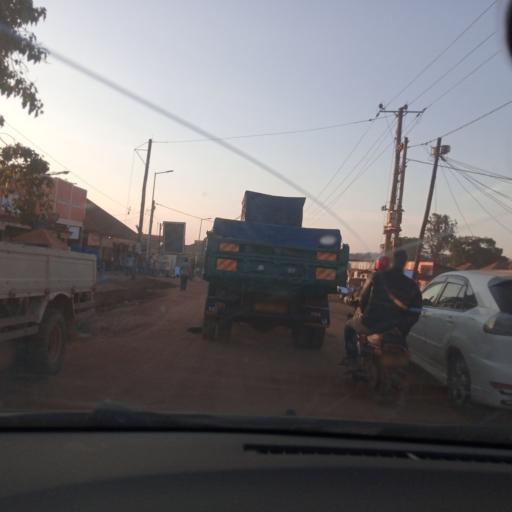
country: UG
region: Central Region
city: Masaka
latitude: -0.3197
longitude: 31.7605
